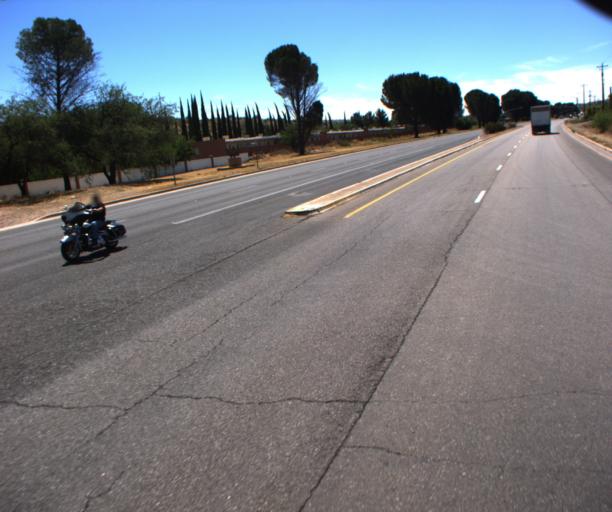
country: US
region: Arizona
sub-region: Santa Cruz County
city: Nogales
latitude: 31.3919
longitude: -110.9544
